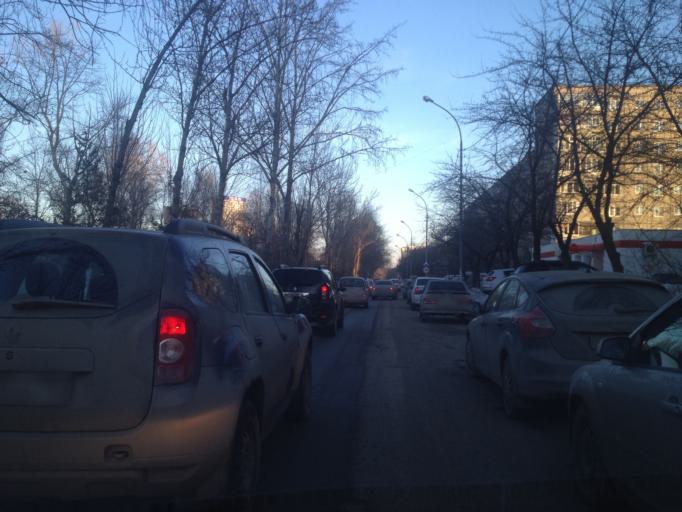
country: RU
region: Sverdlovsk
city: Sovkhoznyy
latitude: 56.8033
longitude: 60.5806
